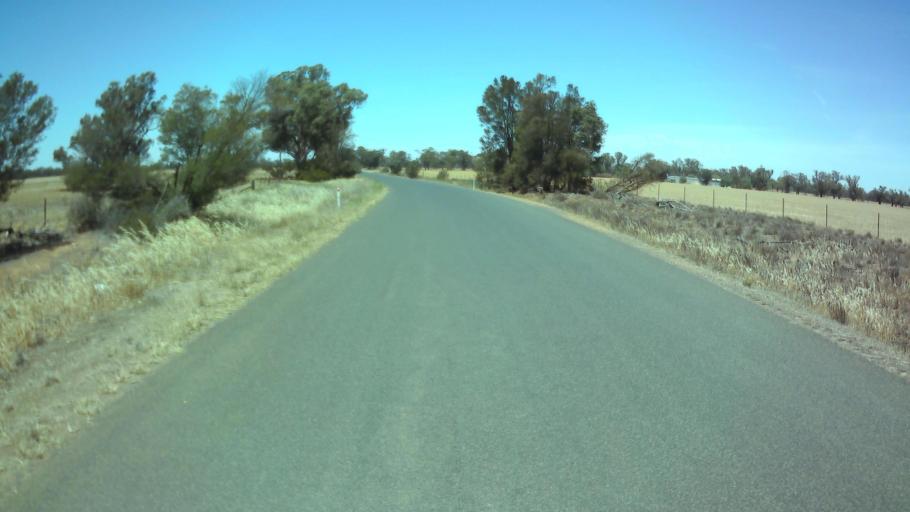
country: AU
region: New South Wales
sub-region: Weddin
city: Grenfell
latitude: -34.0587
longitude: 147.7797
